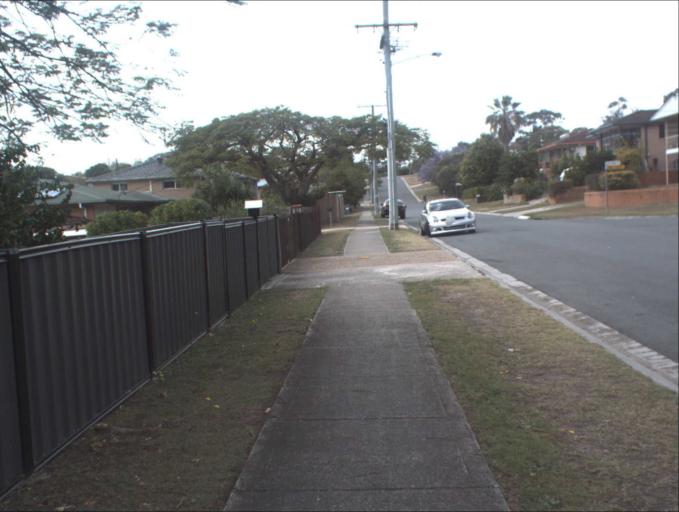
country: AU
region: Queensland
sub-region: Logan
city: Windaroo
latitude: -27.7216
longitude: 153.1902
